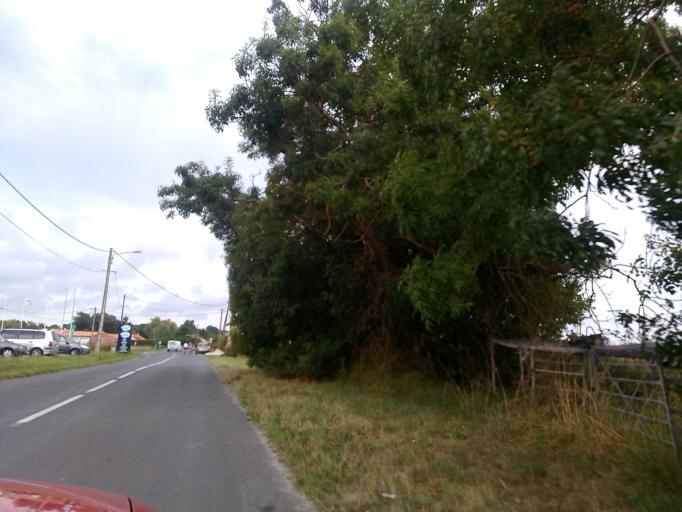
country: FR
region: Poitou-Charentes
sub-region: Departement de la Charente-Maritime
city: La Tremblade
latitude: 45.7736
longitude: -1.1359
